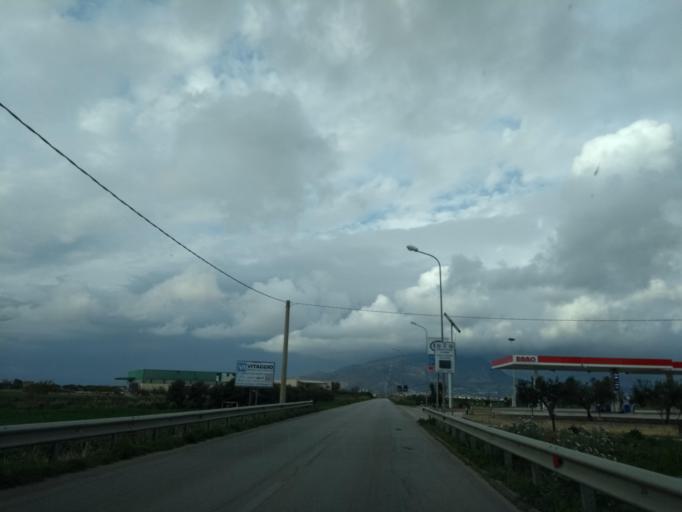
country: IT
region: Sicily
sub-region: Trapani
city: Paceco
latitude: 37.9725
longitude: 12.5247
